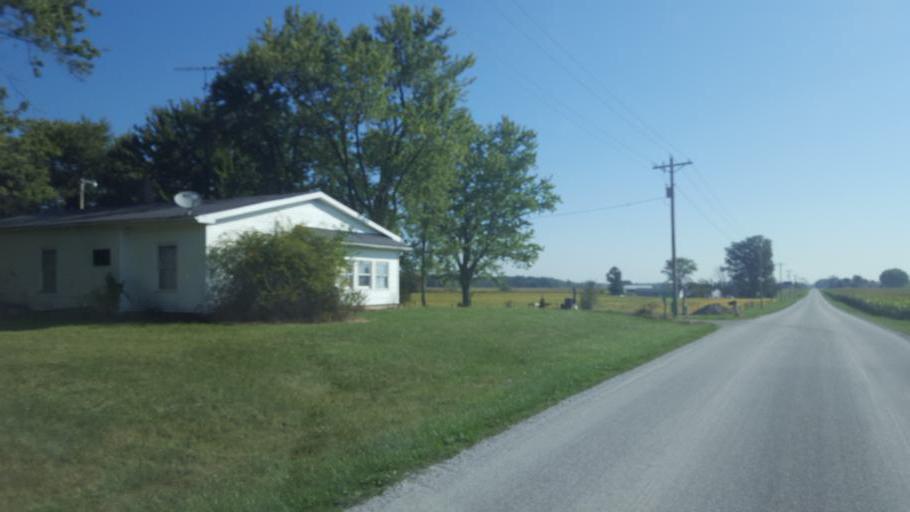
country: US
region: Ohio
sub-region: Hardin County
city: Kenton
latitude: 40.5802
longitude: -83.5555
